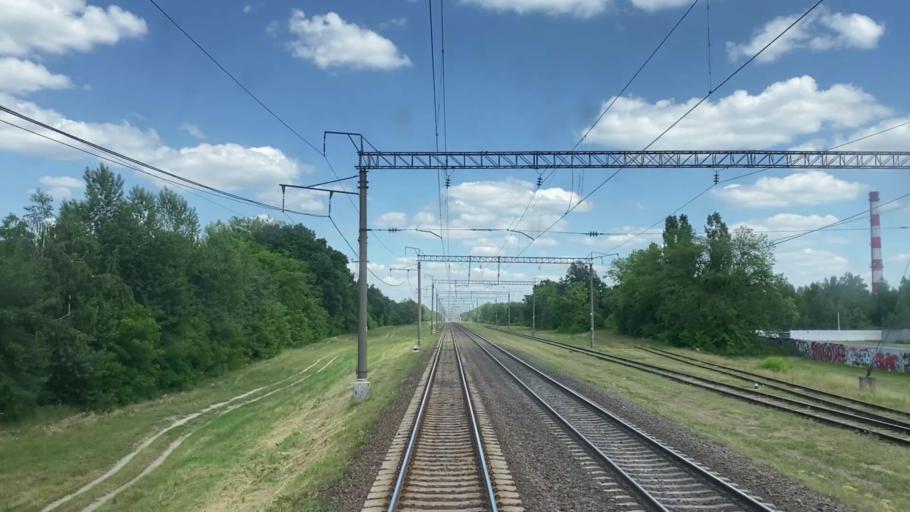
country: BY
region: Brest
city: Brest
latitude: 52.1217
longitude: 23.7798
